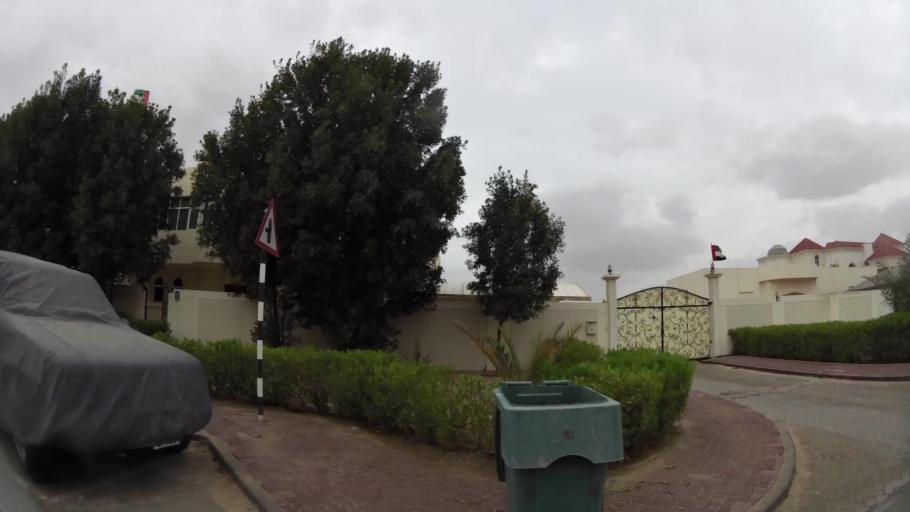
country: AE
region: Abu Dhabi
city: Abu Dhabi
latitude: 24.3768
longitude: 54.6472
